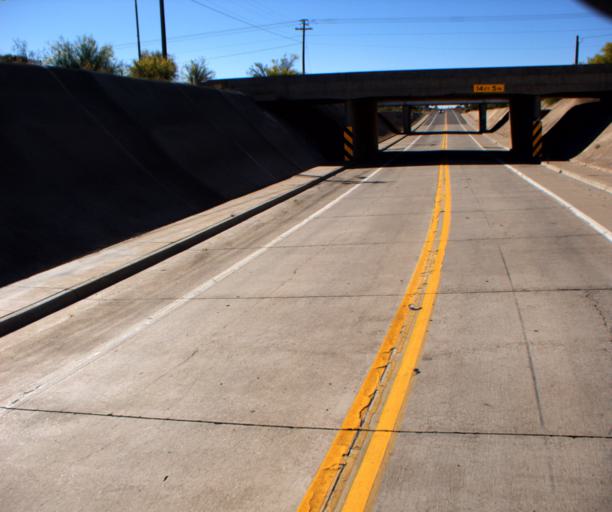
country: US
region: Arizona
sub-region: Maricopa County
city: Gila Bend
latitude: 32.9438
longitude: -112.7350
